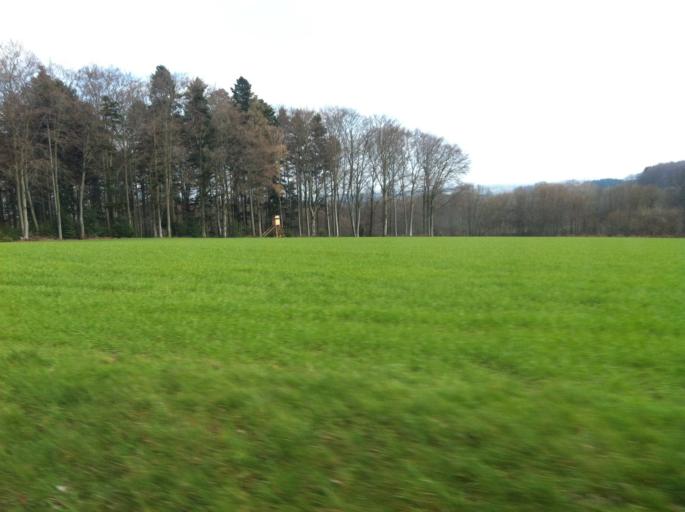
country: DE
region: Baden-Wuerttemberg
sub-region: Karlsruhe Region
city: Limbach
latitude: 49.4575
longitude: 9.1907
